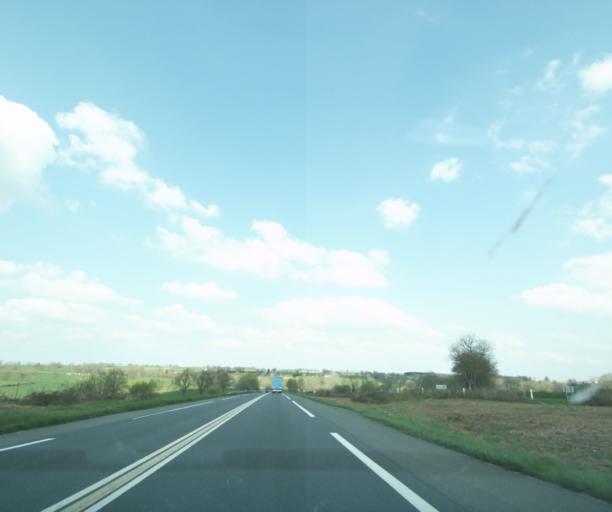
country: FR
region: Auvergne
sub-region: Departement de l'Allier
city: Montmarault
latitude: 46.3362
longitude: 2.9799
